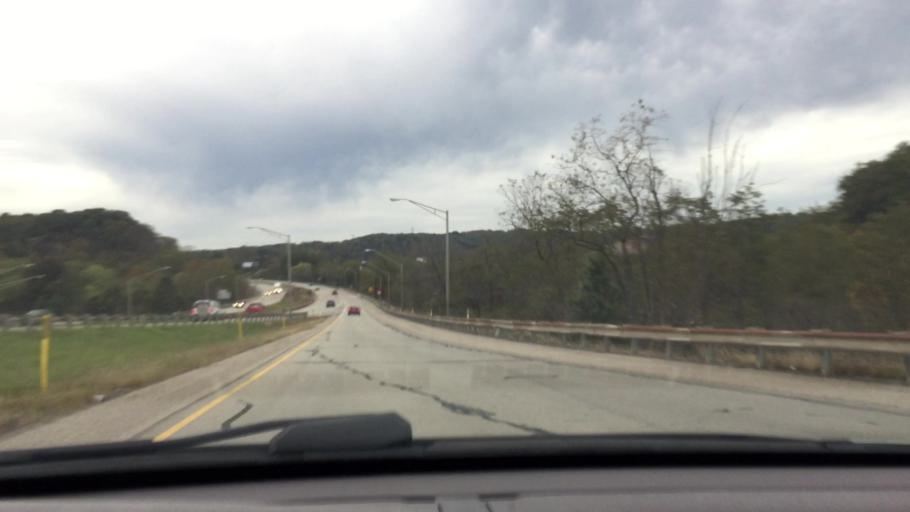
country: US
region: Pennsylvania
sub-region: Beaver County
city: Aliquippa
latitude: 40.6017
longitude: -80.2994
